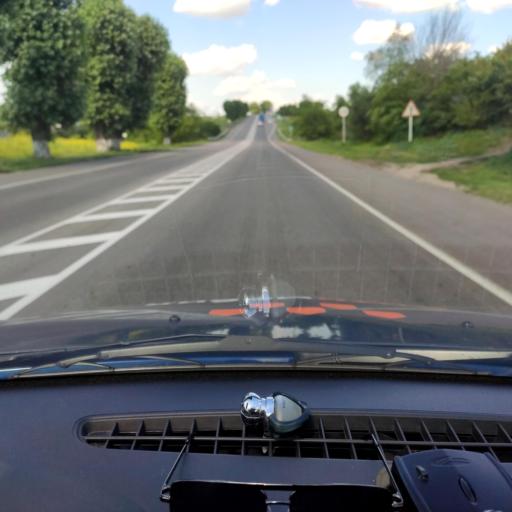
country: RU
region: Voronezj
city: Novovoronezh
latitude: 51.3385
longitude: 39.2700
